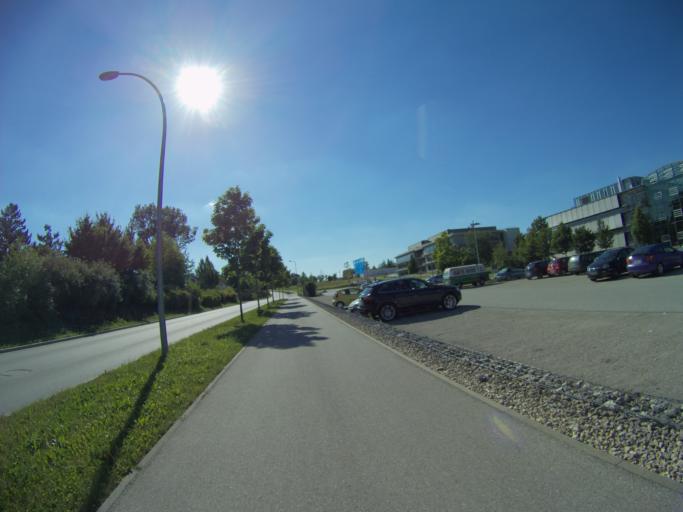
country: DE
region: Bavaria
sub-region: Upper Bavaria
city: Freising
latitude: 48.3982
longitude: 11.7216
